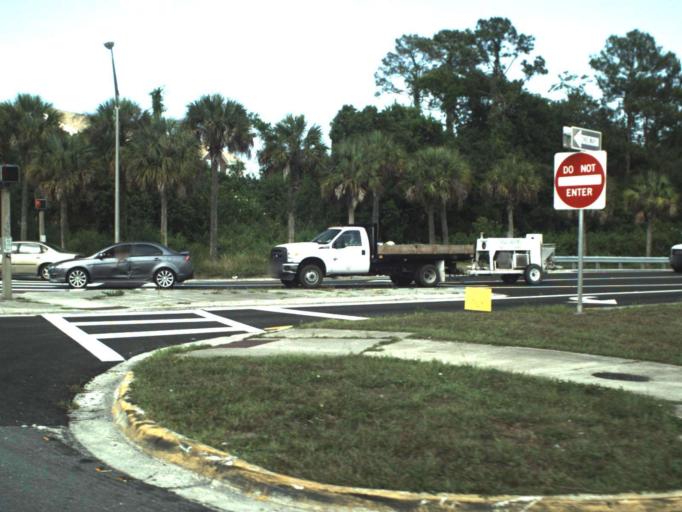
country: US
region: Florida
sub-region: Seminole County
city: Sanford
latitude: 28.7763
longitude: -81.2764
